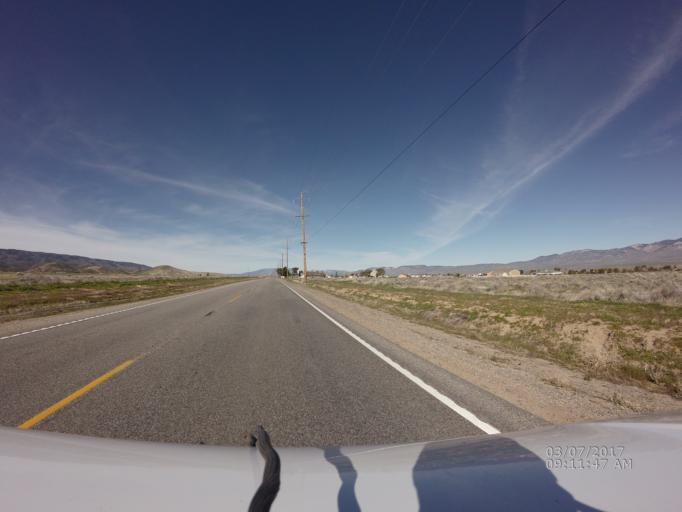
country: US
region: California
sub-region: Los Angeles County
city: Green Valley
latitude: 34.7758
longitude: -118.5819
